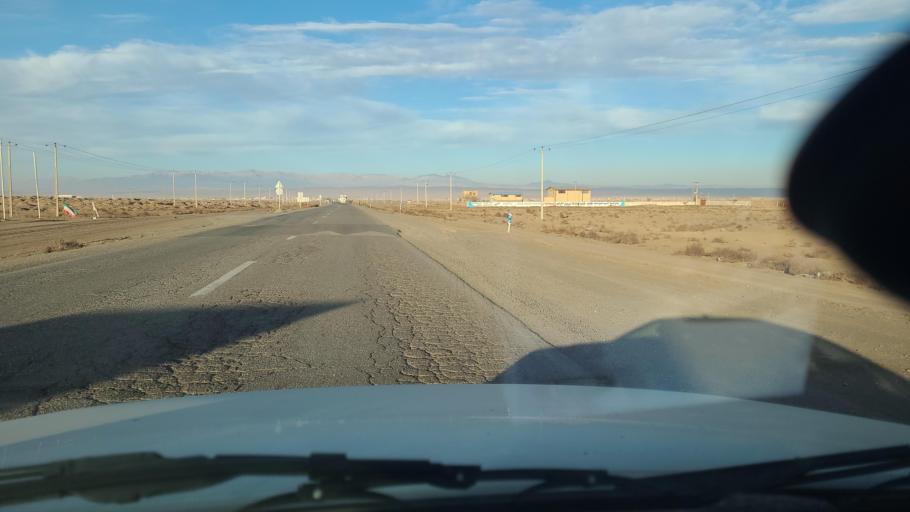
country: IR
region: Razavi Khorasan
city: Neqab
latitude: 36.5881
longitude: 57.5834
